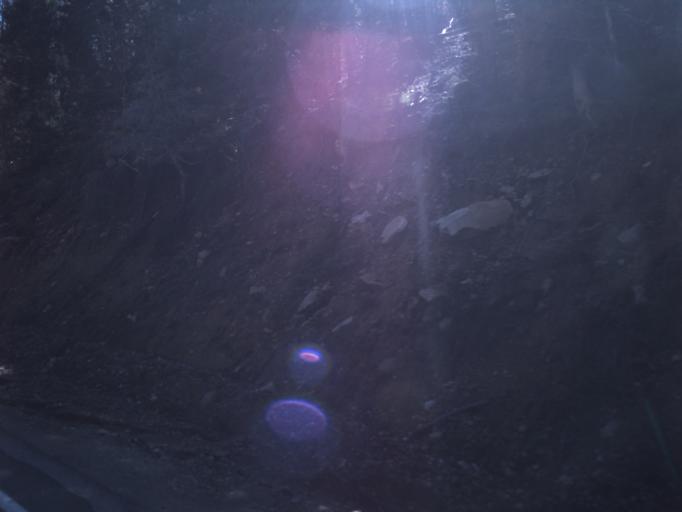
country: US
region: Utah
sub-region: Iron County
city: Parowan
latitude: 37.7313
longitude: -112.8386
